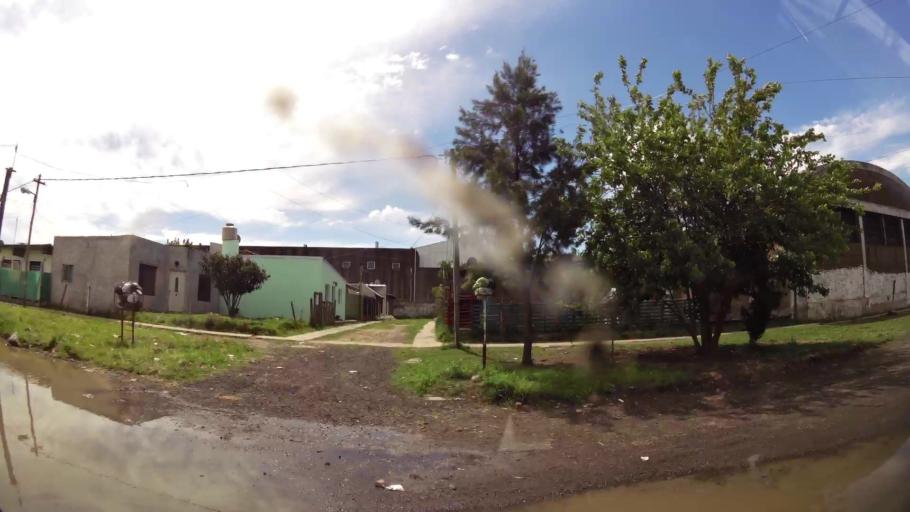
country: AR
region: Buenos Aires
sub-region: Partido de Quilmes
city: Quilmes
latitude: -34.7580
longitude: -58.3017
